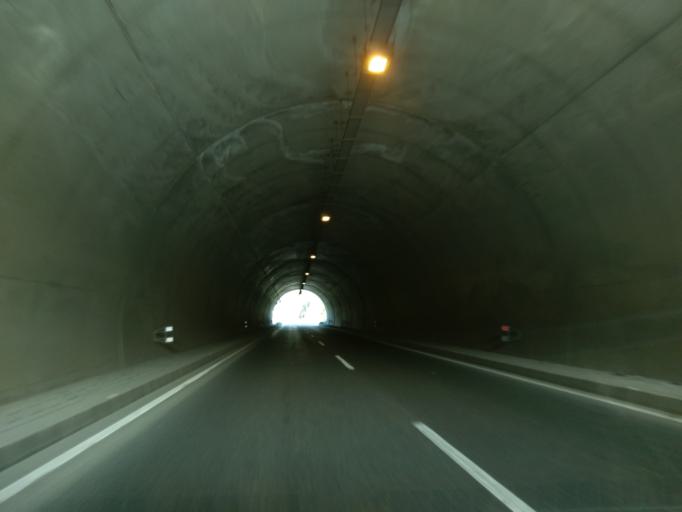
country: TR
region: Ordu
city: Bolaman
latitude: 40.9959
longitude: 37.6381
